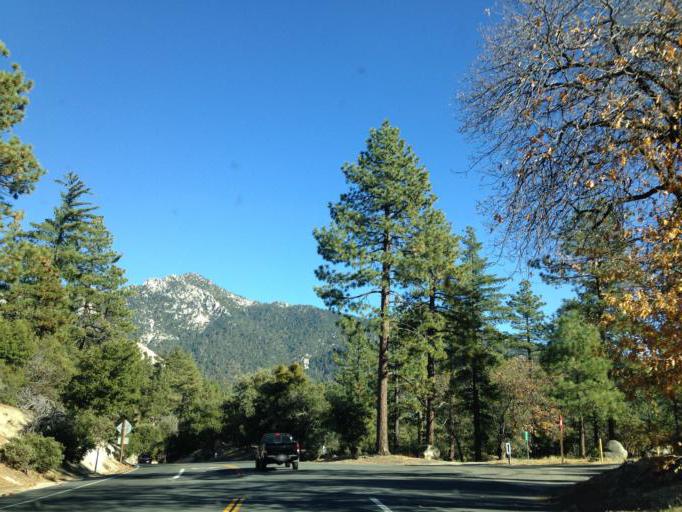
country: US
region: California
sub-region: Riverside County
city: Idyllwild-Pine Cove
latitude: 33.7527
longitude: -116.7220
